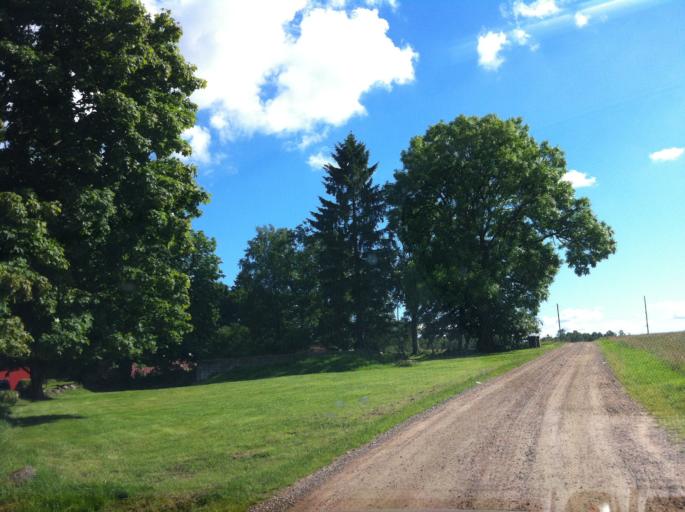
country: SE
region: Skane
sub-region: Astorps Kommun
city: Kvidinge
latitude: 56.0733
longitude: 13.0739
